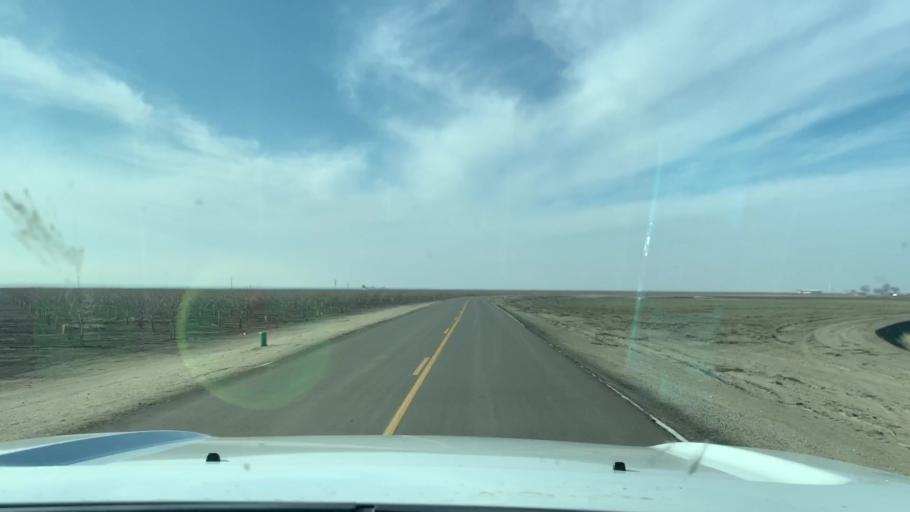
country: US
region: California
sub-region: Kern County
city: Buttonwillow
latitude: 35.4464
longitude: -119.5566
